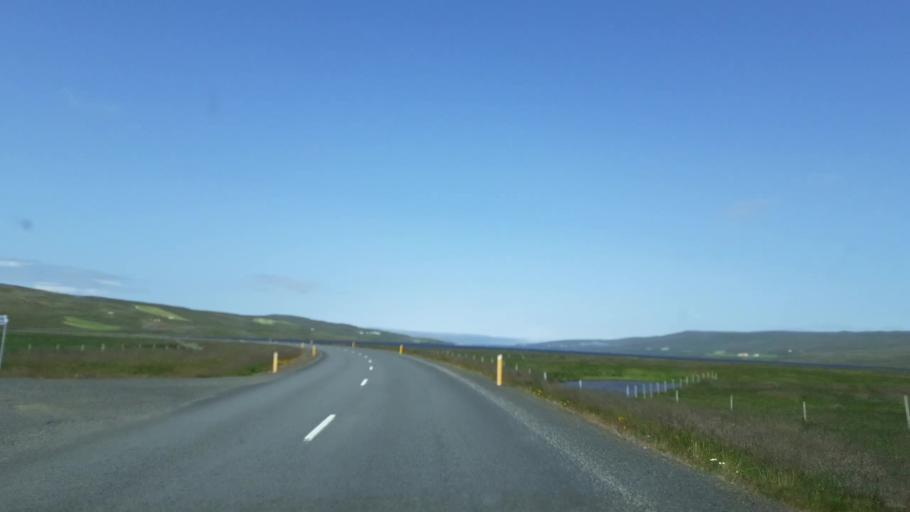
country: IS
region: West
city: Borgarnes
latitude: 65.1518
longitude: -21.0803
